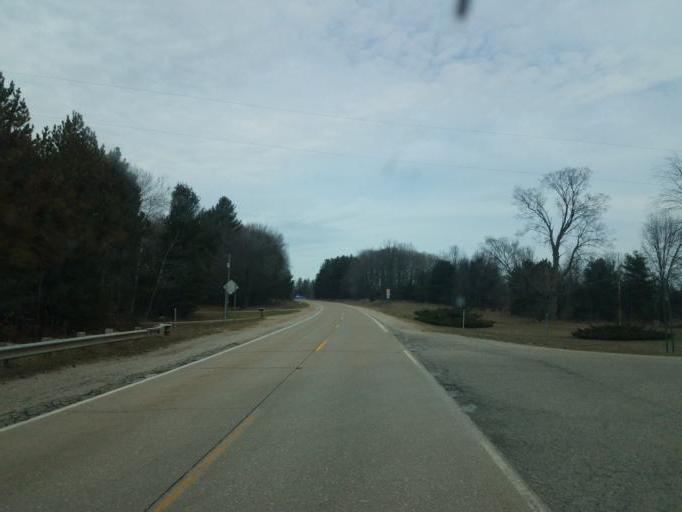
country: US
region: Michigan
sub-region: Oceana County
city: Hart
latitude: 43.7965
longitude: -86.3593
